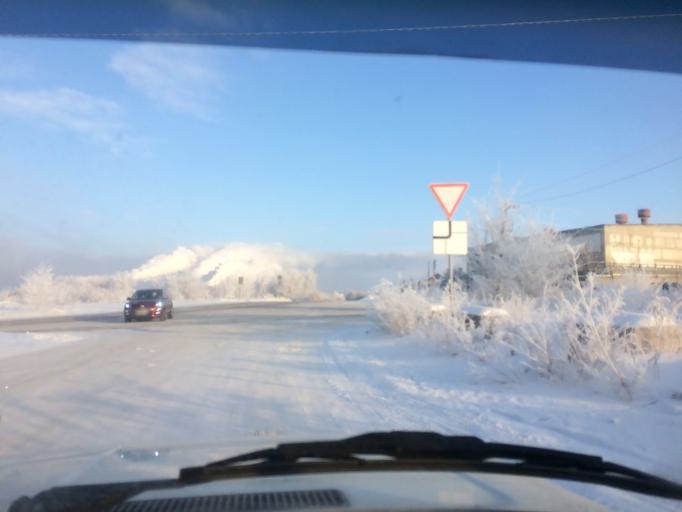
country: RU
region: Chelyabinsk
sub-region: Gorod Magnitogorsk
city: Magnitogorsk
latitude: 53.3949
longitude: 59.0846
